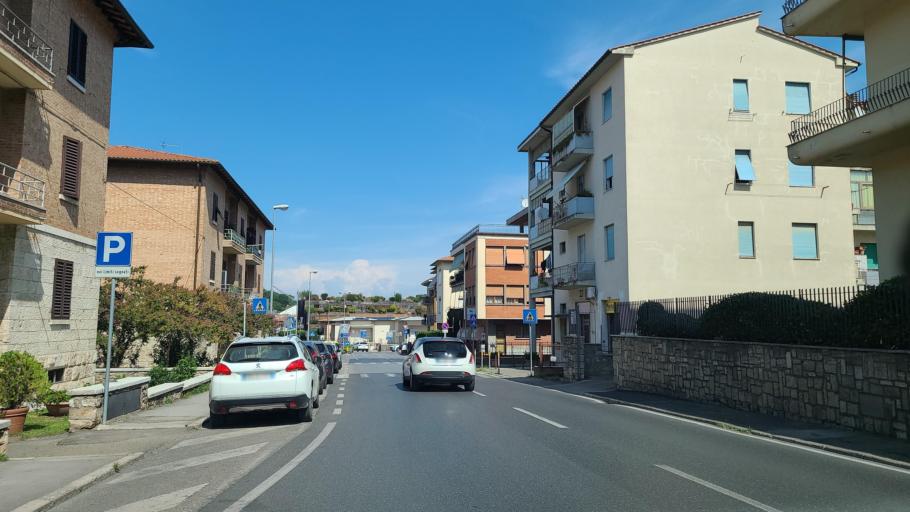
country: IT
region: Tuscany
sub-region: Provincia di Siena
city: Colle di Val d'Elsa
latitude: 43.4207
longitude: 11.1294
